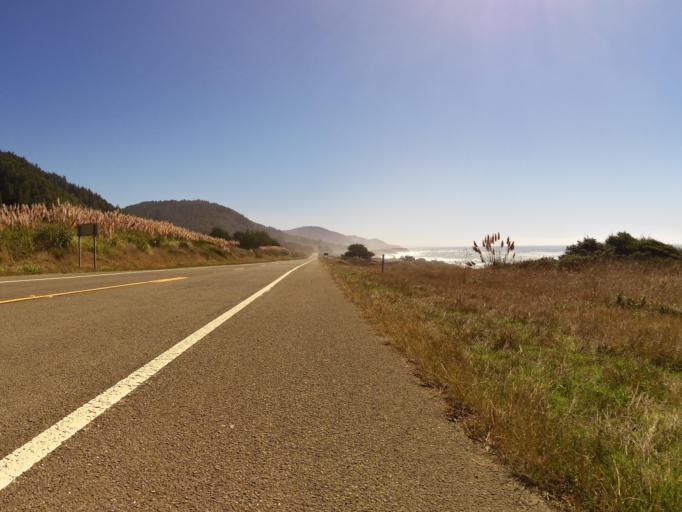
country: US
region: California
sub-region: Mendocino County
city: Fort Bragg
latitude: 39.6884
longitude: -123.7929
